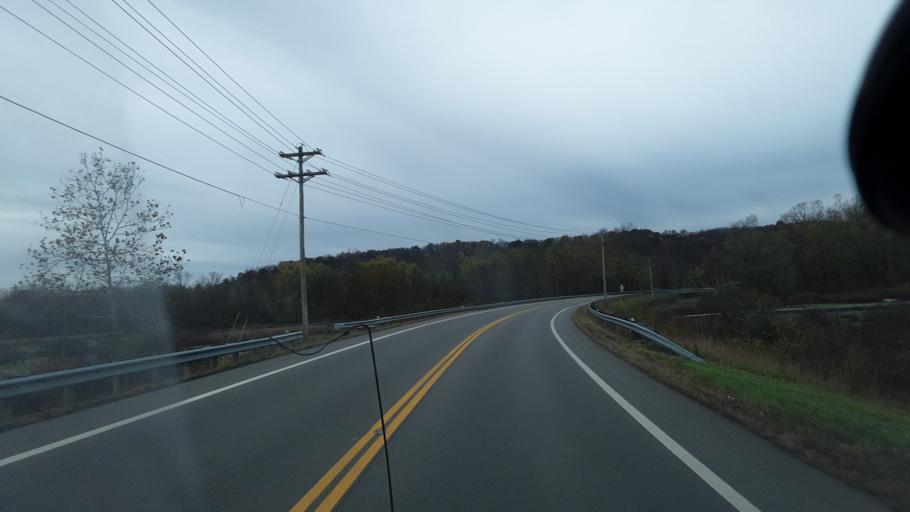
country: US
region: Ohio
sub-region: Holmes County
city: Millersburg
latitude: 40.4830
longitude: -81.9831
